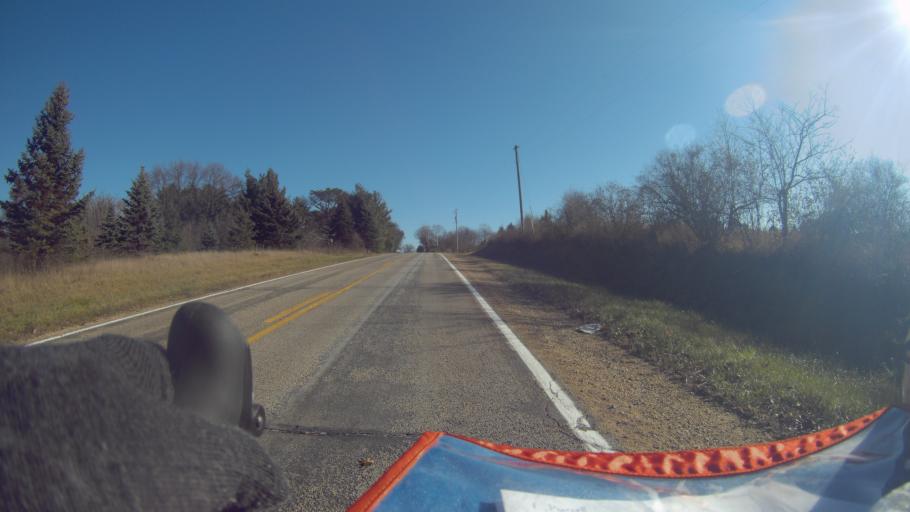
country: US
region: Wisconsin
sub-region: Dane County
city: Fitchburg
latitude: 42.8969
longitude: -89.4576
